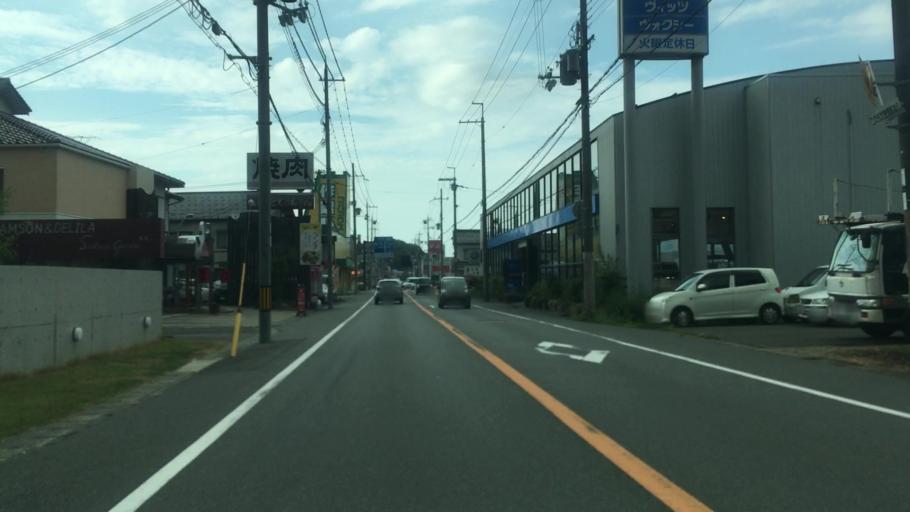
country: JP
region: Hyogo
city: Toyooka
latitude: 35.5264
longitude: 134.8210
